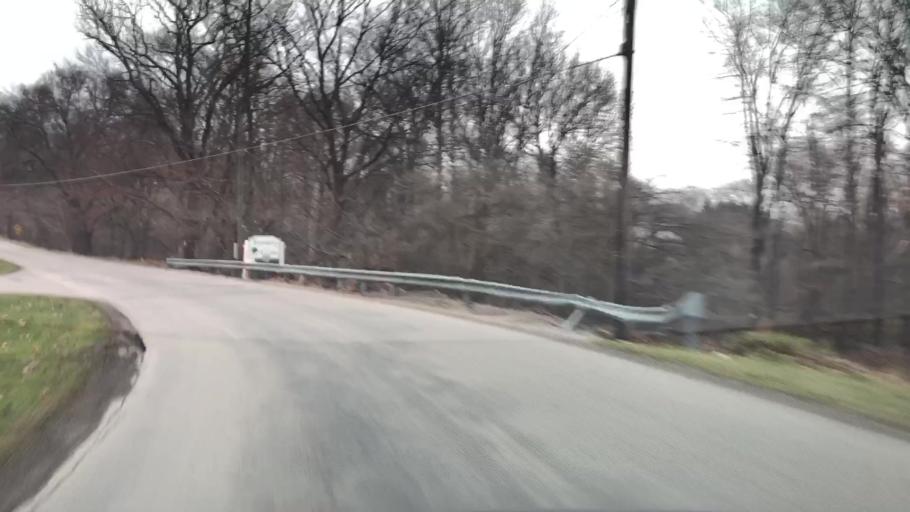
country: US
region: Pennsylvania
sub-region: Mercer County
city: Grove City
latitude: 41.1301
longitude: -80.0916
